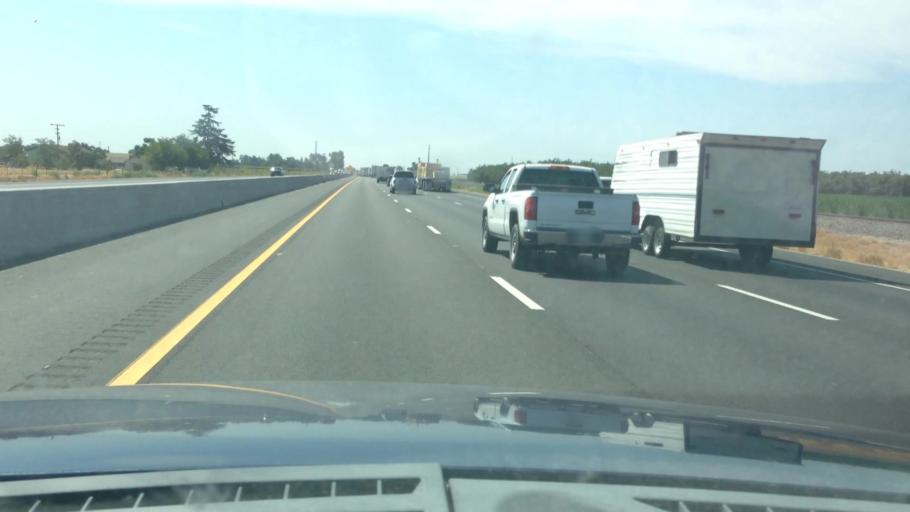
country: US
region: California
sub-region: Tulare County
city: Goshen
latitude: 36.2898
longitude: -119.3799
